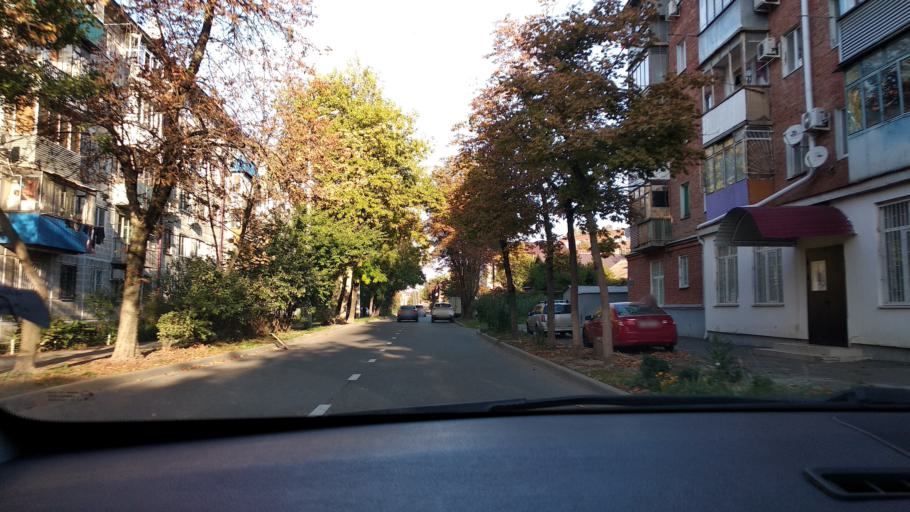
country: RU
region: Adygeya
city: Yablonovskiy
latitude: 45.0105
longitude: 38.9628
